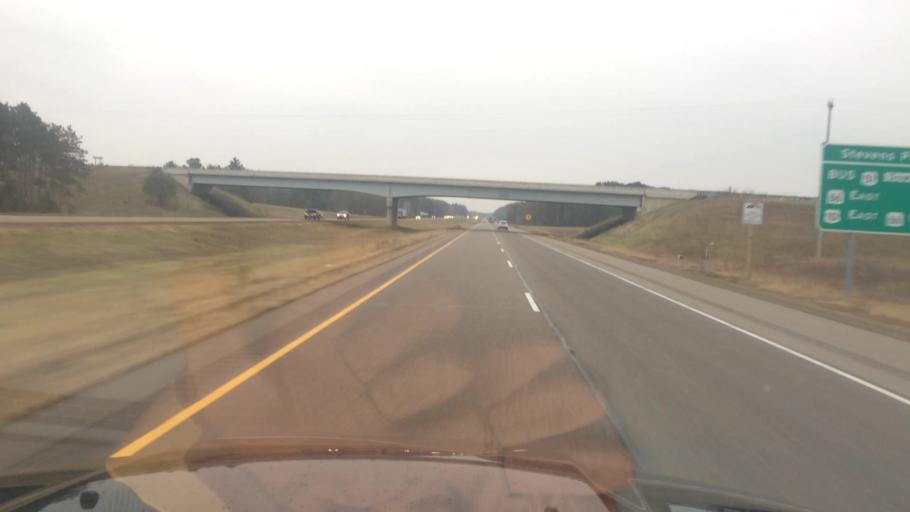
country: US
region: Wisconsin
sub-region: Portage County
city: Stevens Point
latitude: 44.5712
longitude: -89.5995
